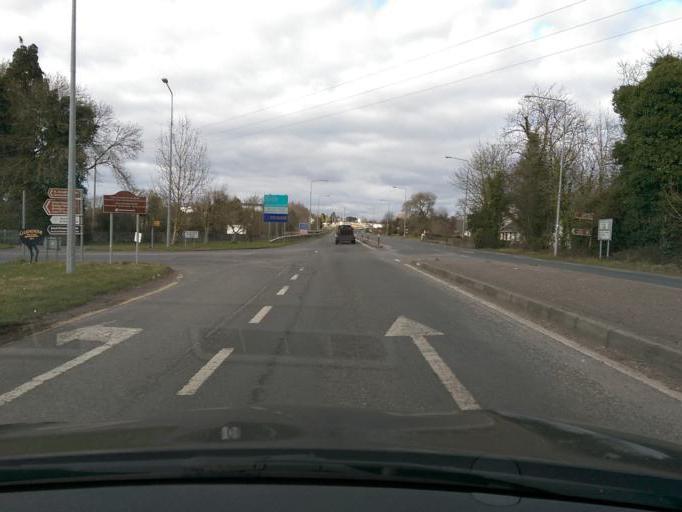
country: IE
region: Leinster
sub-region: An Iarmhi
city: Athlone
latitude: 53.4112
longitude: -7.9845
